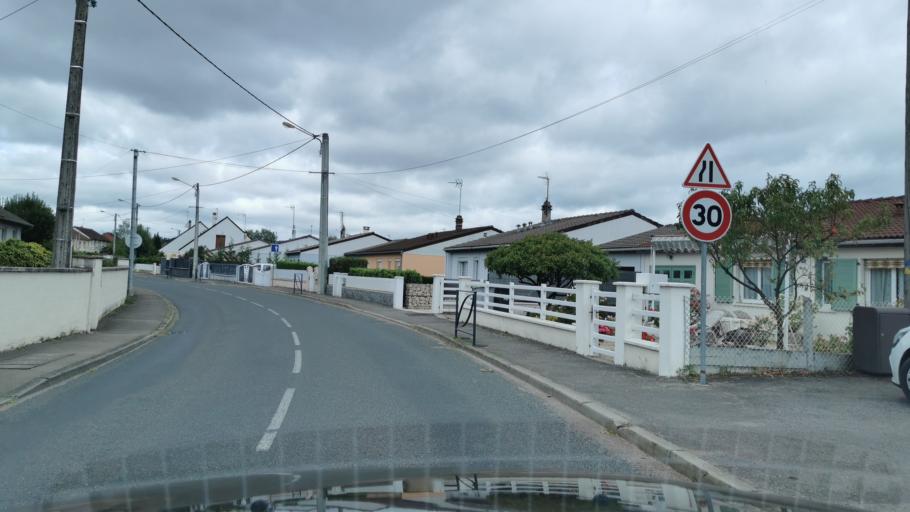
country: FR
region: Bourgogne
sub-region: Departement de Saone-et-Loire
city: Le Breuil
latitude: 46.8031
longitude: 4.4713
